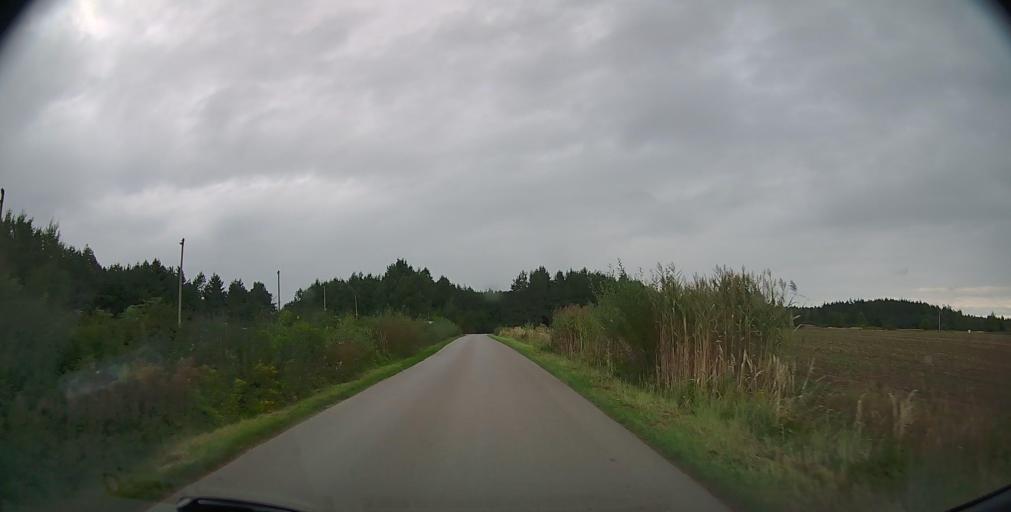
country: PL
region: Masovian Voivodeship
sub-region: Powiat radomski
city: Jedlinsk
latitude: 51.4579
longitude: 21.1039
